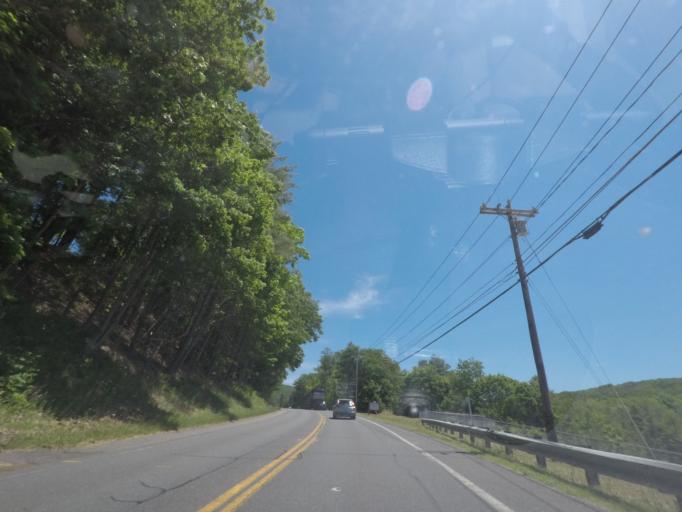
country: US
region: Massachusetts
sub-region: Berkshire County
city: Lee
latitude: 42.2949
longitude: -73.1740
